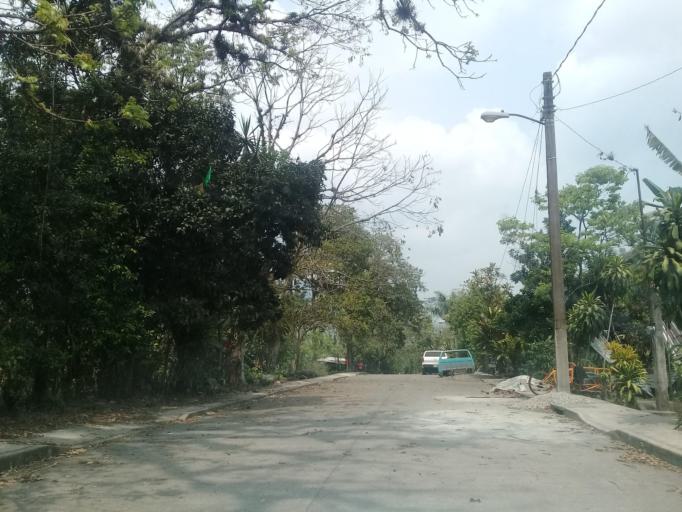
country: MX
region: Veracruz
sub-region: Cordoba
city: San Jose de Tapia
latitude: 18.8267
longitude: -96.9794
